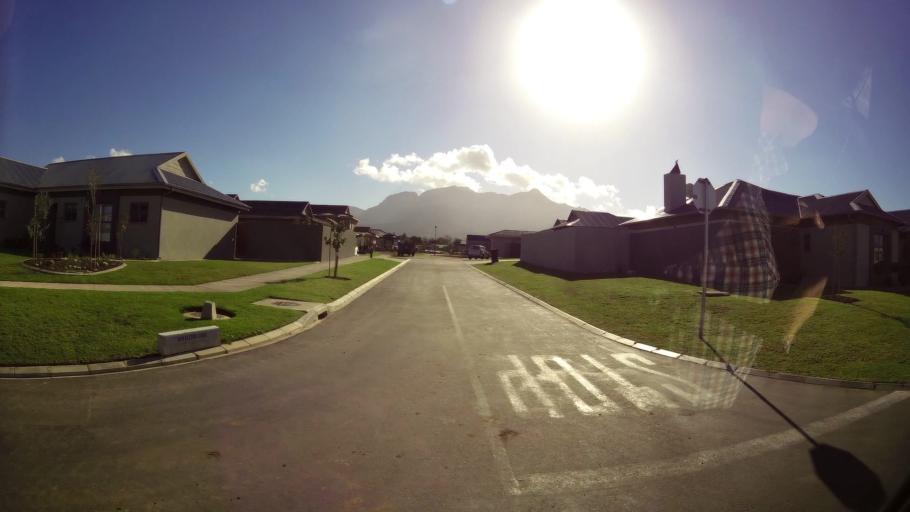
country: ZA
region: Western Cape
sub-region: Eden District Municipality
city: George
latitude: -33.9614
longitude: 22.4207
